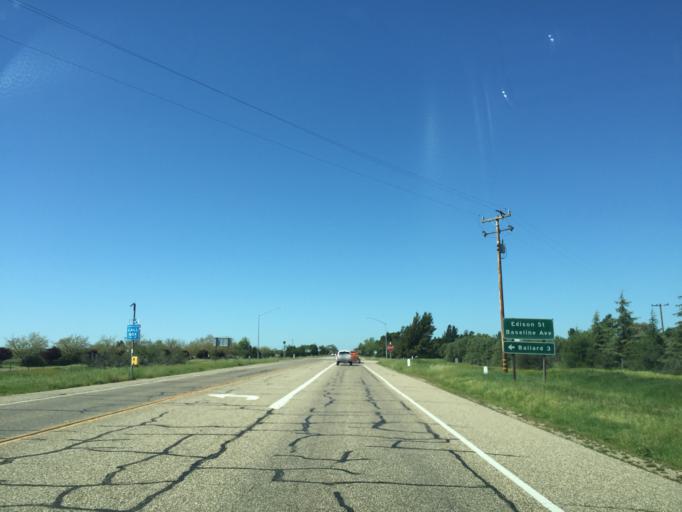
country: US
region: California
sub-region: Santa Barbara County
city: Santa Ynez
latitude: 34.6328
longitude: -120.0802
